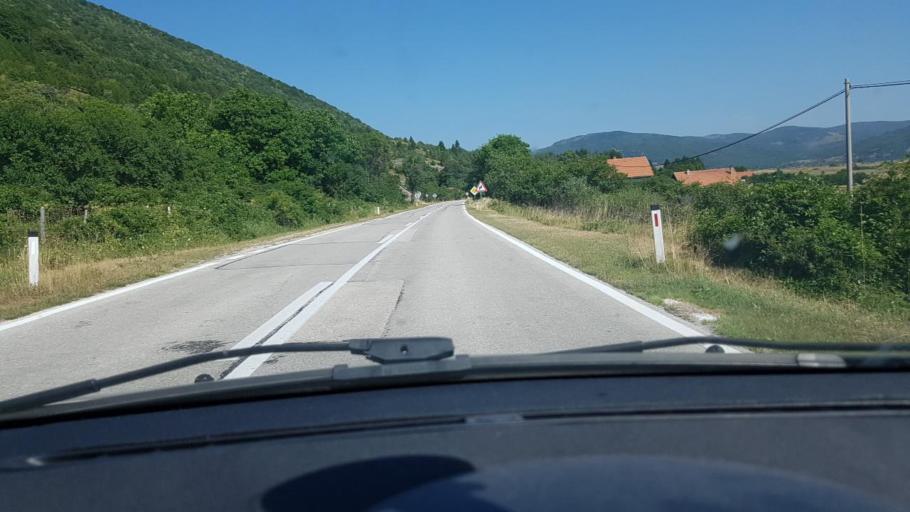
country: BA
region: Federation of Bosnia and Herzegovina
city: Bosansko Grahovo
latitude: 44.2564
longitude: 16.3047
